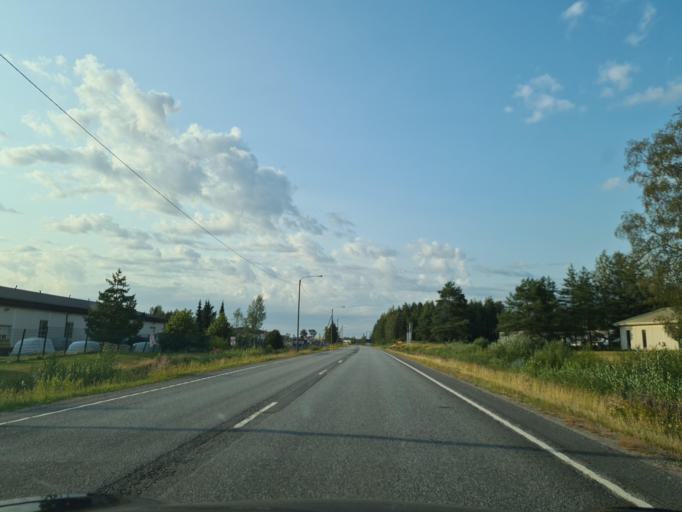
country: FI
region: Southern Ostrobothnia
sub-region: Seinaejoki
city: Kauhava
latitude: 63.0820
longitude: 23.0587
